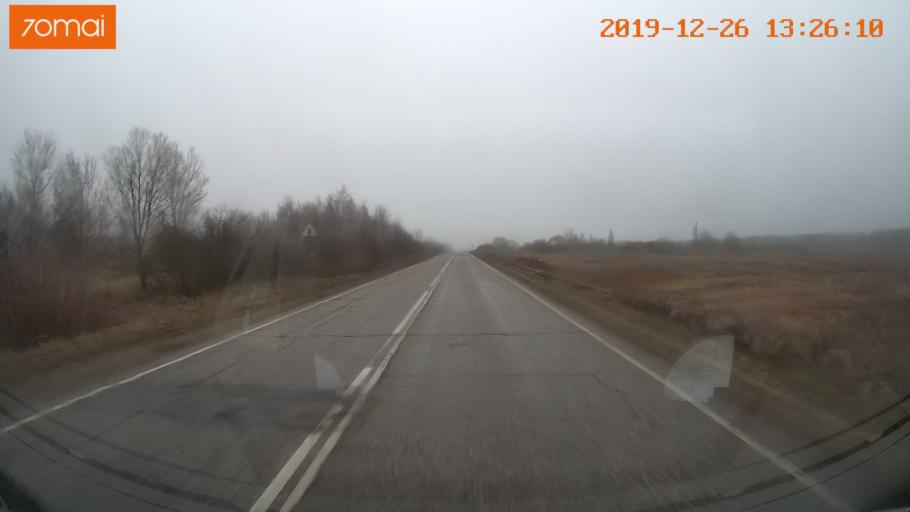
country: RU
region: Vologda
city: Cherepovets
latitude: 58.8674
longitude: 38.2219
